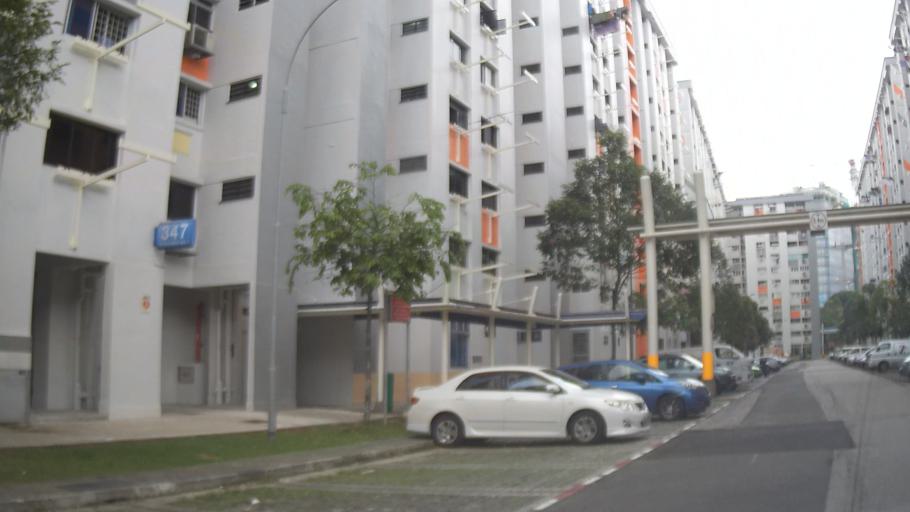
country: MY
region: Johor
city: Johor Bahru
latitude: 1.4327
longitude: 103.7814
